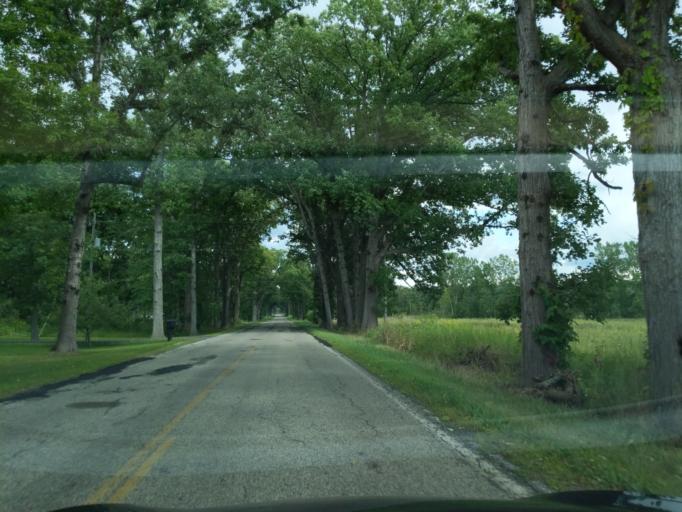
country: US
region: Michigan
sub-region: Eaton County
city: Eaton Rapids
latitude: 42.3787
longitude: -84.5707
